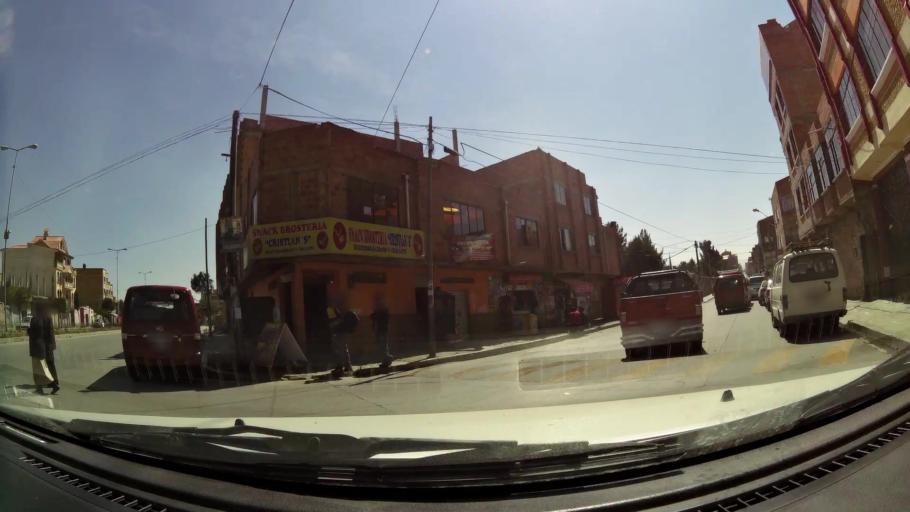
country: BO
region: La Paz
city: La Paz
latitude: -16.5303
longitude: -68.1590
